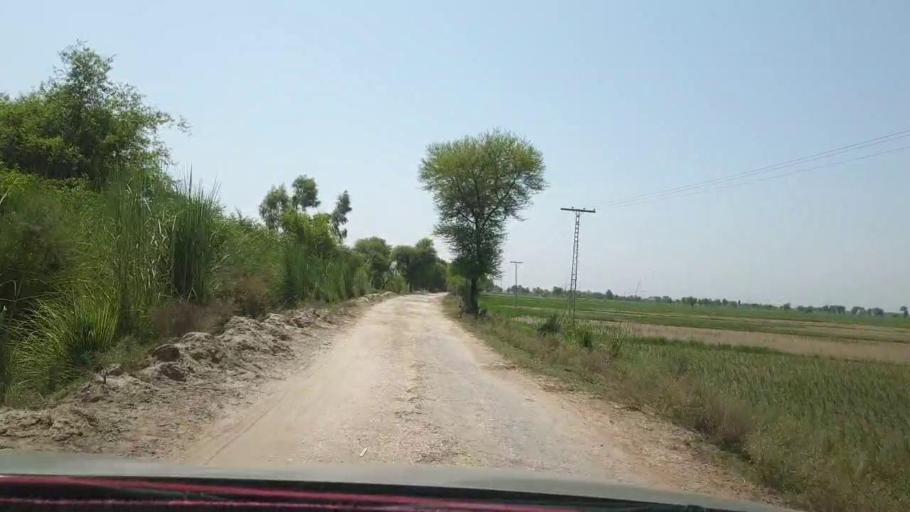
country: PK
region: Sindh
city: Warah
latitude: 27.5048
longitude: 67.7879
